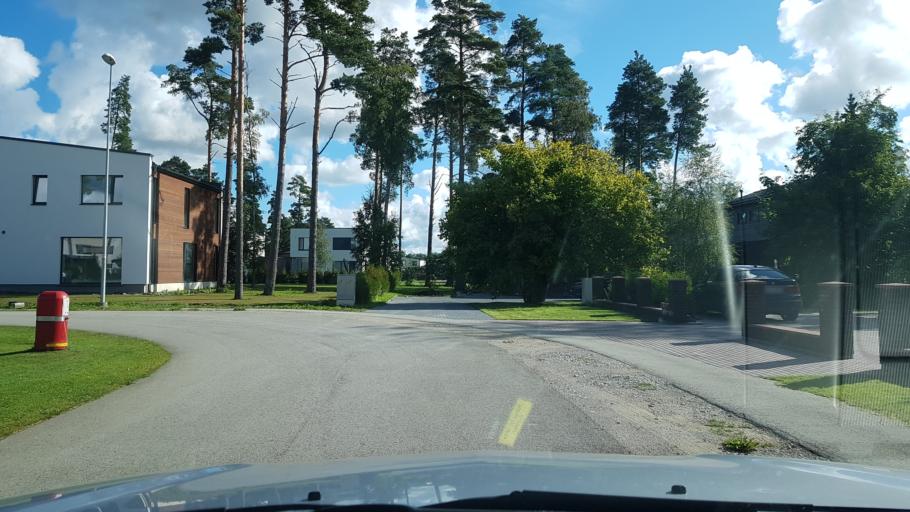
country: EE
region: Harju
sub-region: Kiili vald
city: Kiili
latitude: 59.3585
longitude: 24.8178
